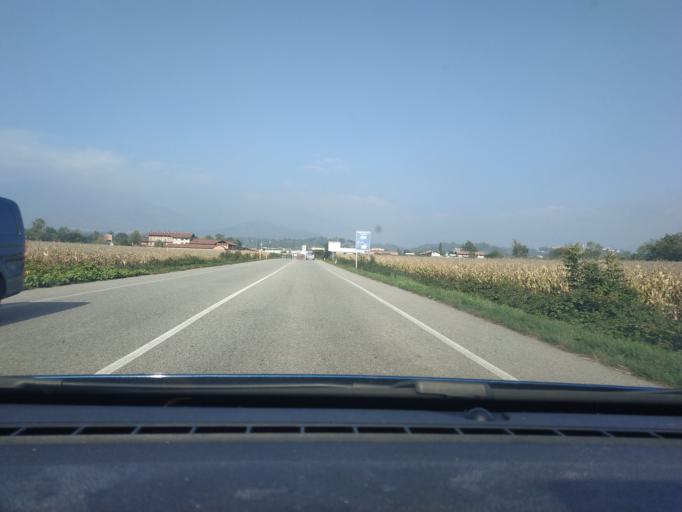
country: IT
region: Piedmont
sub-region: Provincia di Biella
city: Occhieppo Inferiore
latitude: 45.5432
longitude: 8.0373
